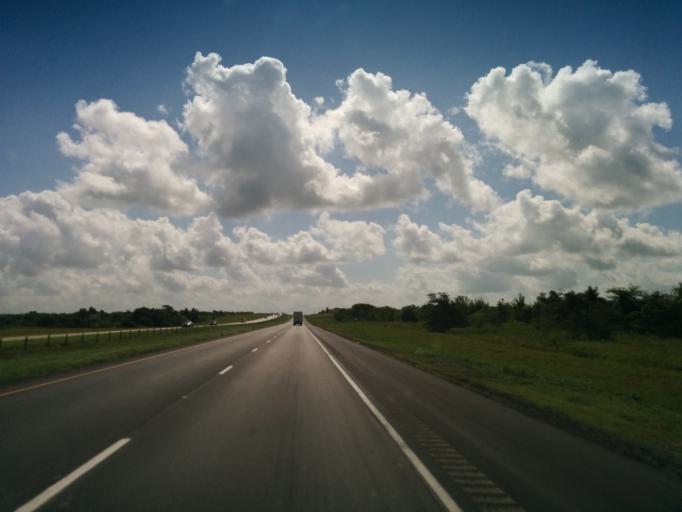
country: US
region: Texas
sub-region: Colorado County
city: Weimar
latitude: 29.6884
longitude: -96.8211
